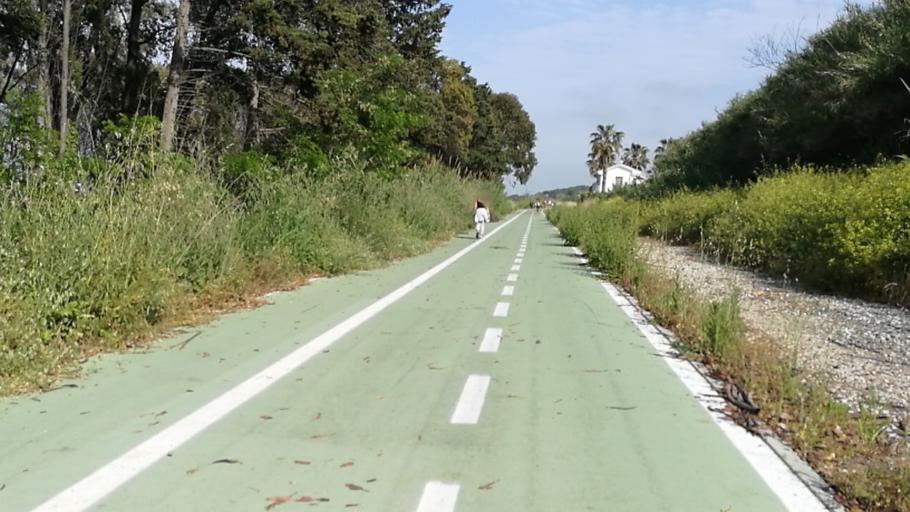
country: IT
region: Abruzzo
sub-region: Provincia di Chieti
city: Casalbordino-Miracoli
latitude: 42.2054
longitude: 14.6020
